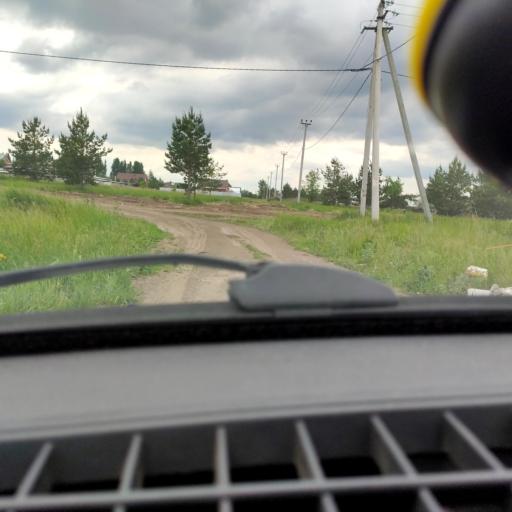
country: RU
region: Samara
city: Povolzhskiy
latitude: 53.5965
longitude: 49.5806
